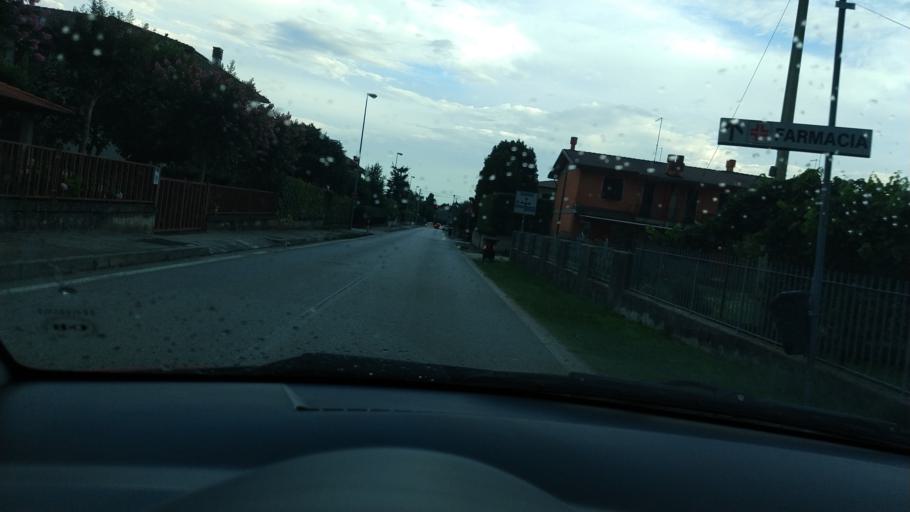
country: IT
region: Veneto
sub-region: Provincia di Vicenza
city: Fara Vicentino
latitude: 45.7391
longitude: 11.5385
